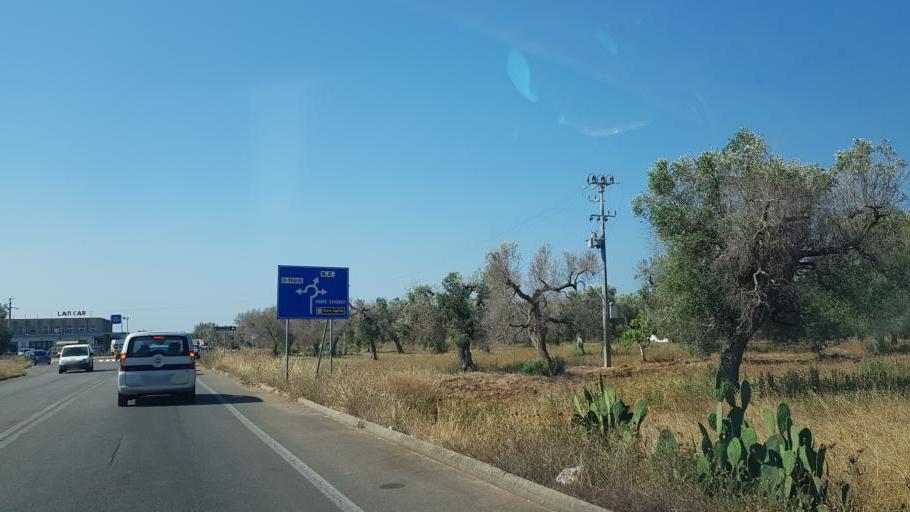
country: IT
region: Apulia
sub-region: Provincia di Lecce
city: Veglie
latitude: 40.3314
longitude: 17.9429
